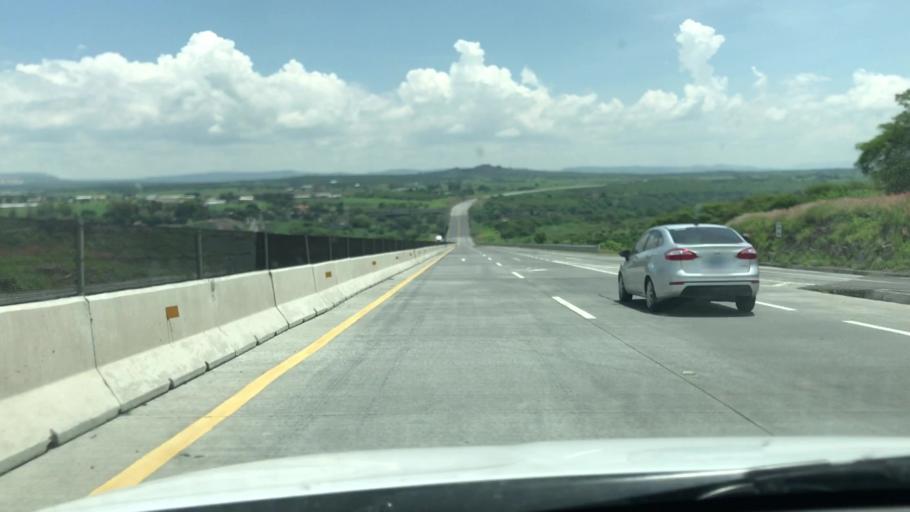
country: MX
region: Jalisco
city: Degollado
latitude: 20.3713
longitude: -102.1262
